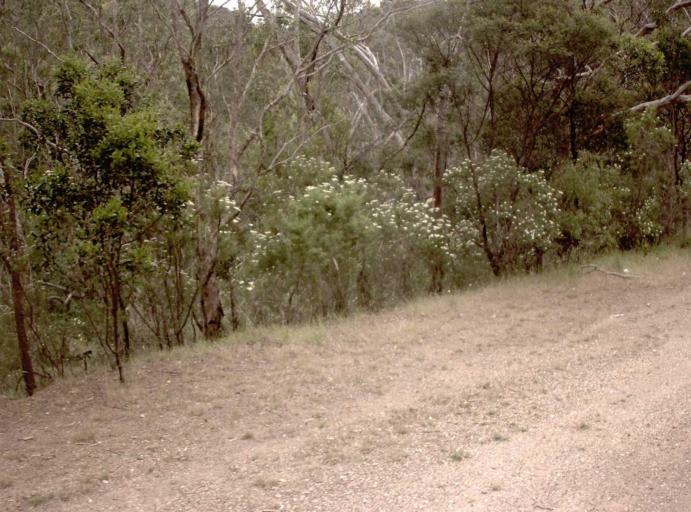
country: AU
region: Victoria
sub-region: East Gippsland
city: Bairnsdale
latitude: -37.5267
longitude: 147.2302
